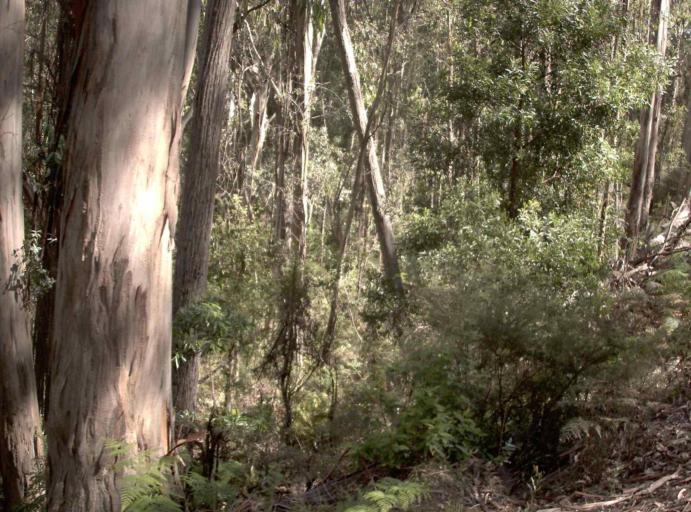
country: AU
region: New South Wales
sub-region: Bombala
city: Bombala
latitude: -37.2900
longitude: 148.7131
